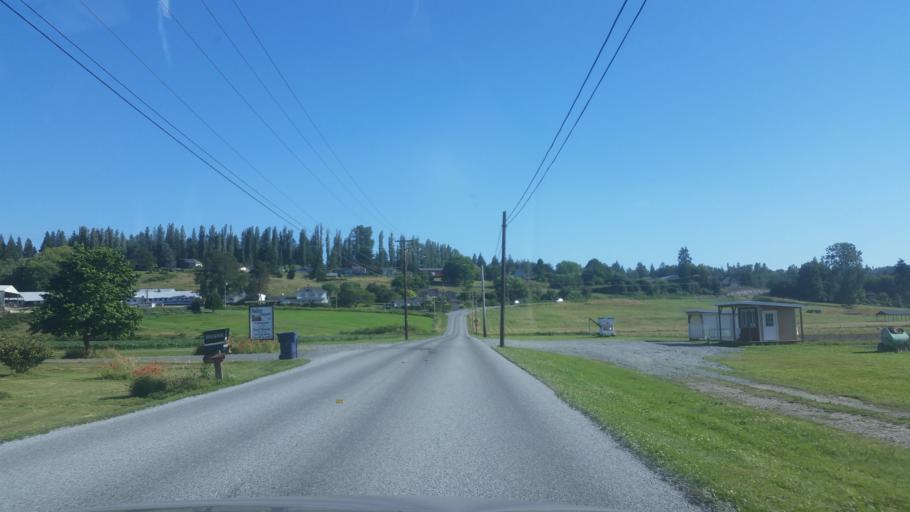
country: US
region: Washington
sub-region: Snohomish County
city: Snohomish
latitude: 47.8810
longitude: -122.0990
